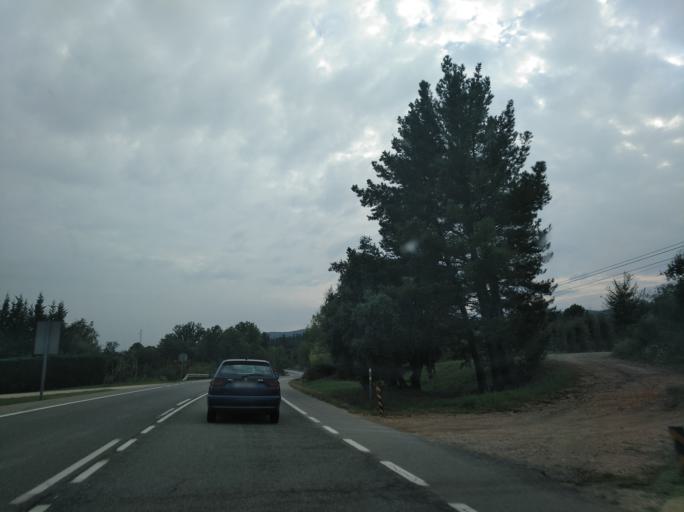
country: ES
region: Catalonia
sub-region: Provincia de Girona
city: Santa Coloma de Farners
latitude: 41.8812
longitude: 2.6583
